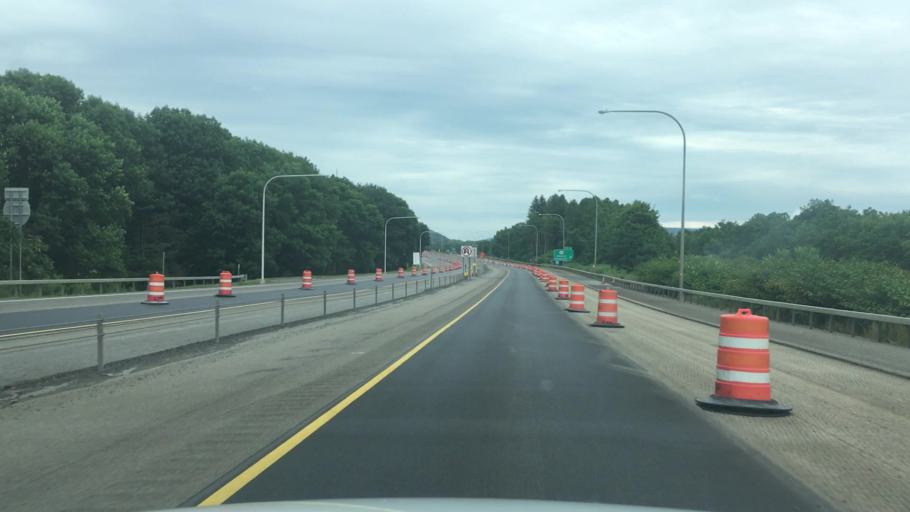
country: US
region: New York
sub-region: Otsego County
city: Oneonta
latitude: 42.4476
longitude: -75.0598
